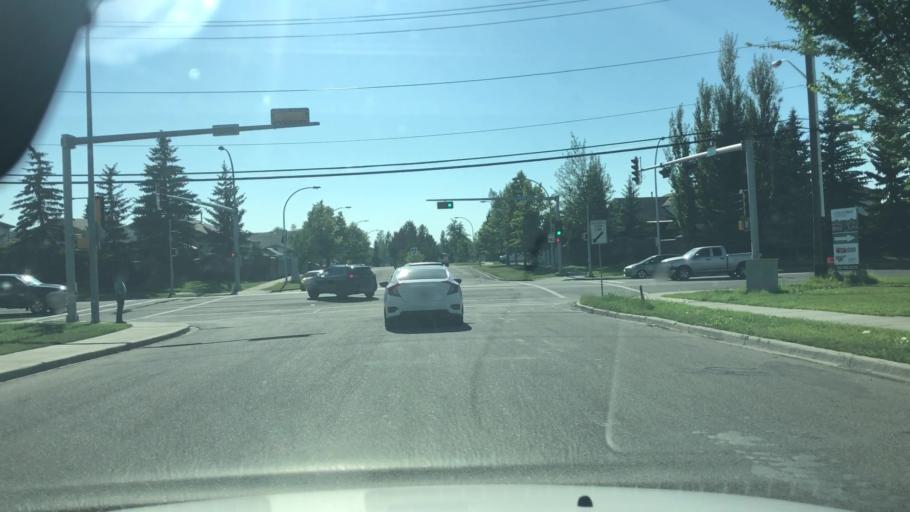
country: CA
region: Alberta
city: Edmonton
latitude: 53.6105
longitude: -113.5405
